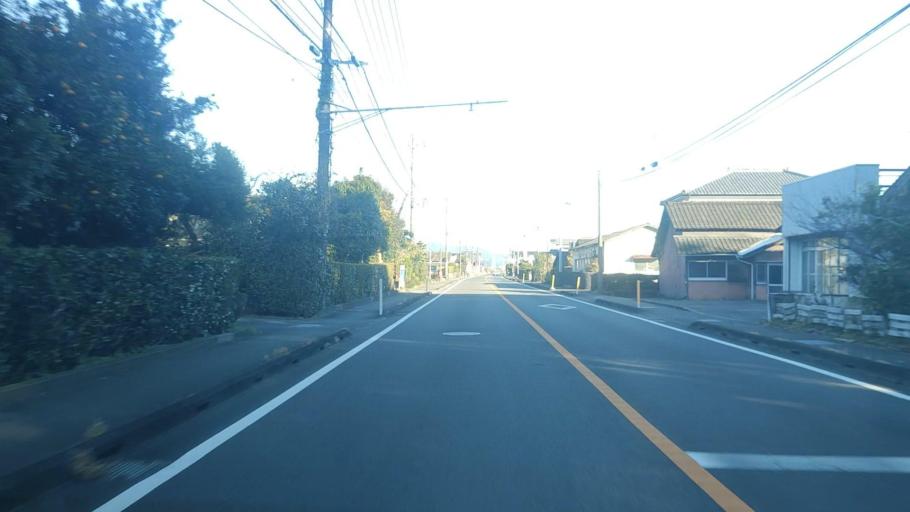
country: JP
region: Miyazaki
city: Nobeoka
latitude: 32.3824
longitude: 131.6276
